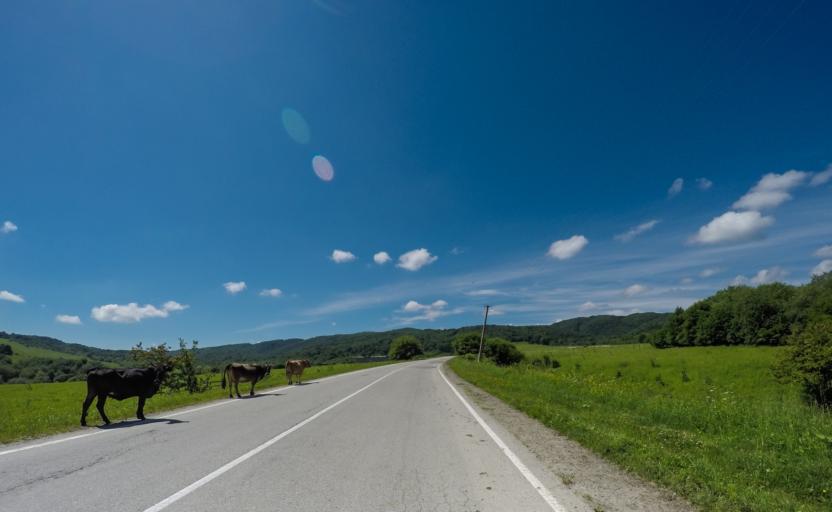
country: RU
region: Kabardino-Balkariya
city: Belaya Rechka
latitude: 43.3994
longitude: 43.5907
